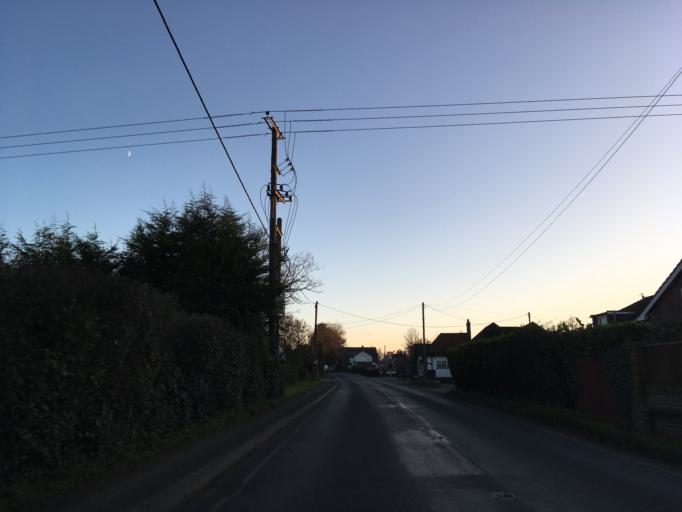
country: GB
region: England
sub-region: Hampshire
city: Colden Common
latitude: 50.9768
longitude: -1.3028
